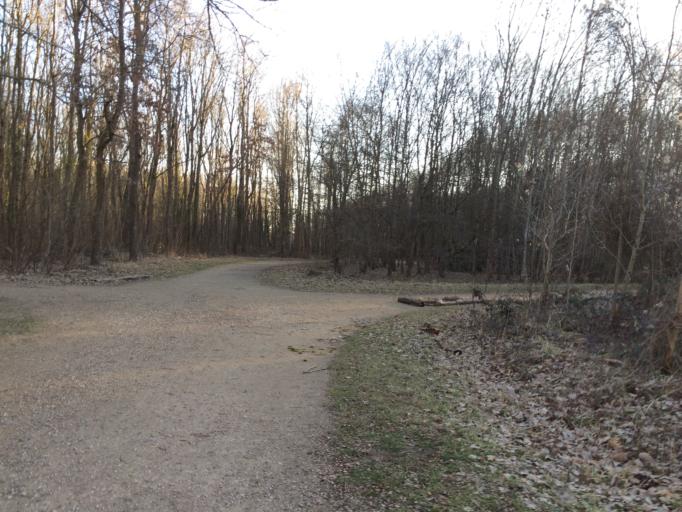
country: FR
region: Ile-de-France
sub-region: Departement de l'Essonne
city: Villebon-sur-Yvette
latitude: 48.7172
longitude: 2.2268
